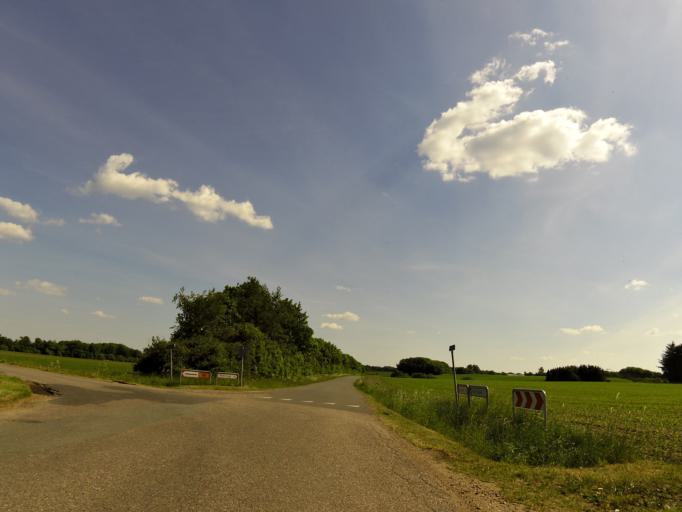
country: DK
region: Central Jutland
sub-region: Holstebro Kommune
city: Vinderup
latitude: 56.4327
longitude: 8.8913
